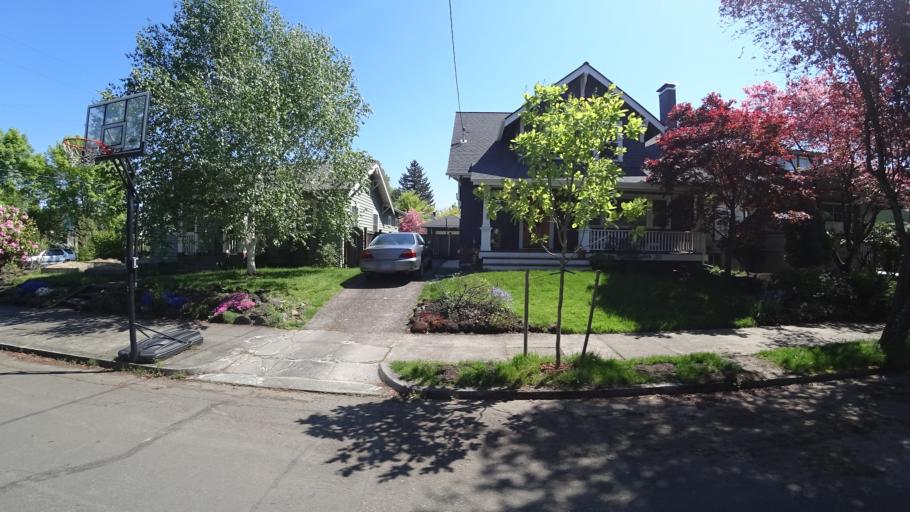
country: US
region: Oregon
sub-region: Clackamas County
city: Milwaukie
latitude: 45.4774
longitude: -122.6452
